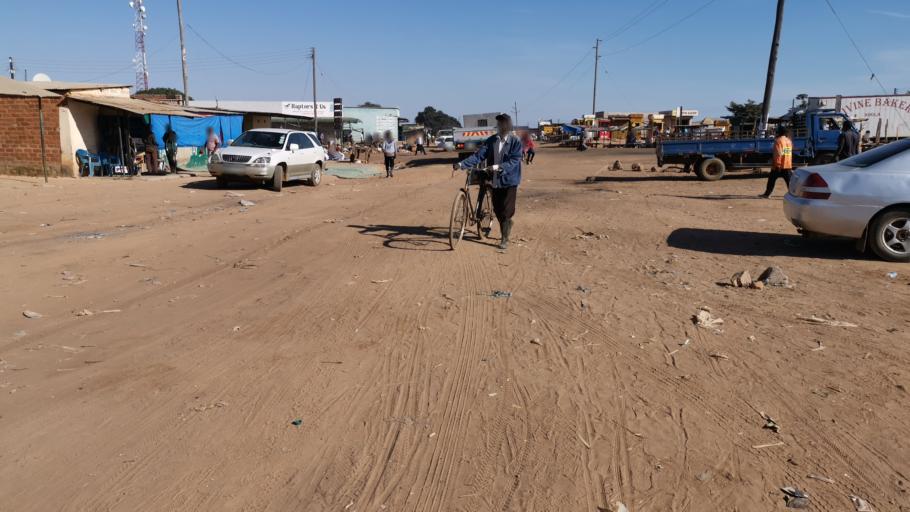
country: ZM
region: Central
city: Mkushi
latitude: -13.9427
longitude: 29.3883
